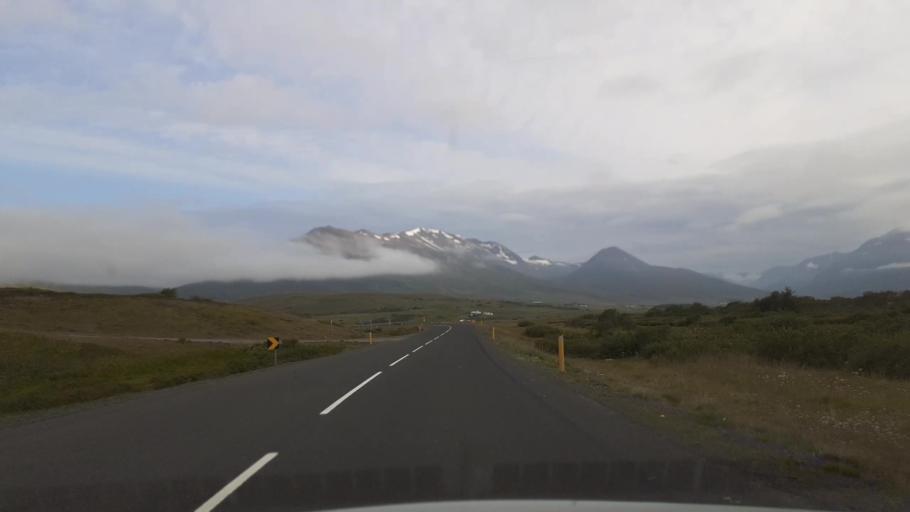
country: IS
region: Northeast
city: Dalvik
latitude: 65.9590
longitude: -18.5380
